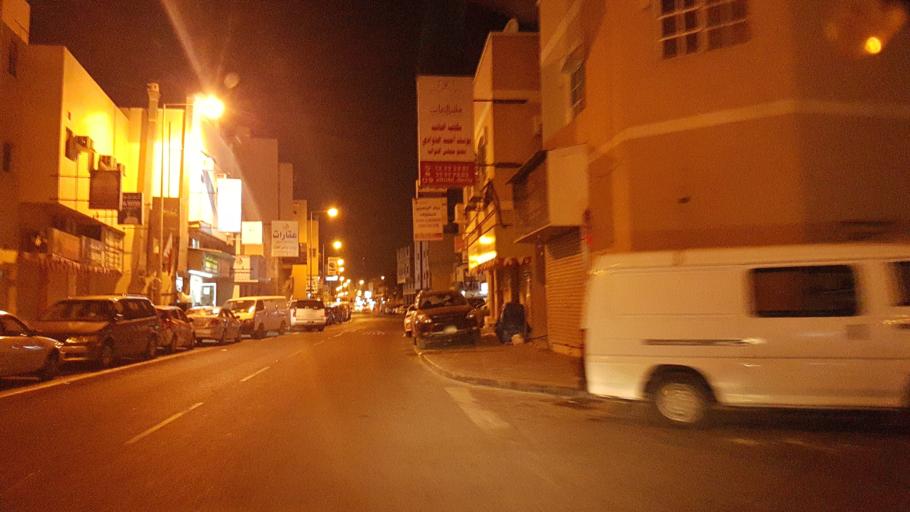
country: BH
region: Muharraq
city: Al Hadd
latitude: 26.2437
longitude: 50.6556
